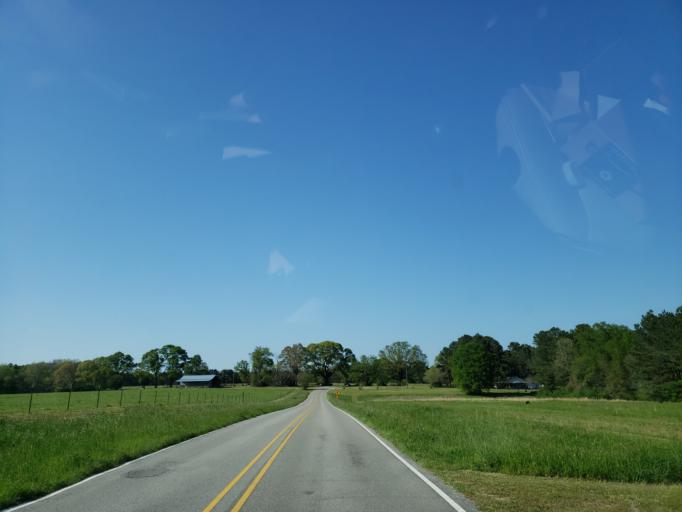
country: US
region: Mississippi
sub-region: Jones County
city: Ellisville
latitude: 31.5917
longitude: -89.3790
